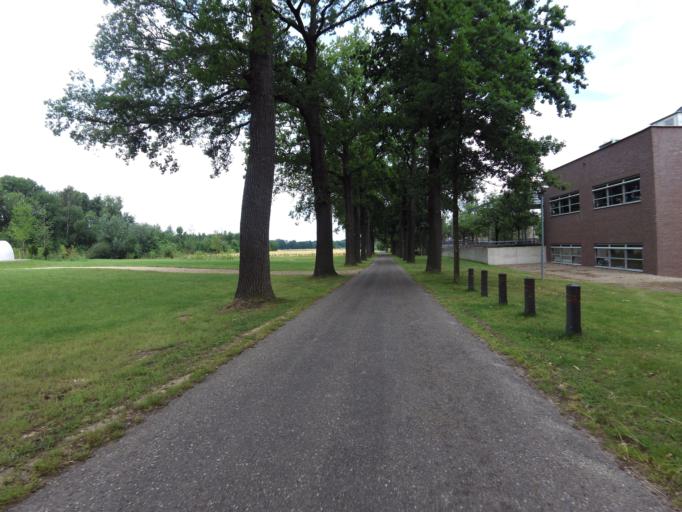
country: NL
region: Limburg
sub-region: Gemeente Heerlen
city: Heerlen
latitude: 50.8809
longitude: 5.9581
